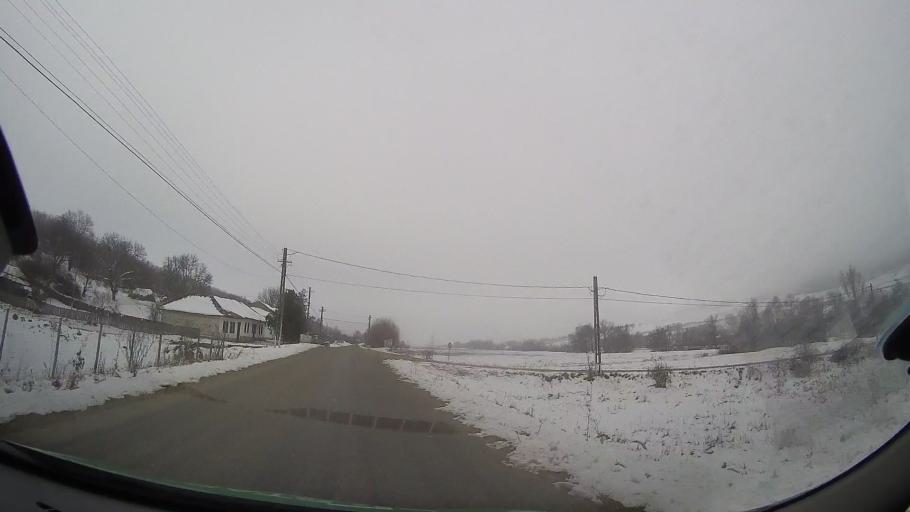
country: RO
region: Bacau
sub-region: Comuna Vultureni
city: Vultureni
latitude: 46.3270
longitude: 27.2916
